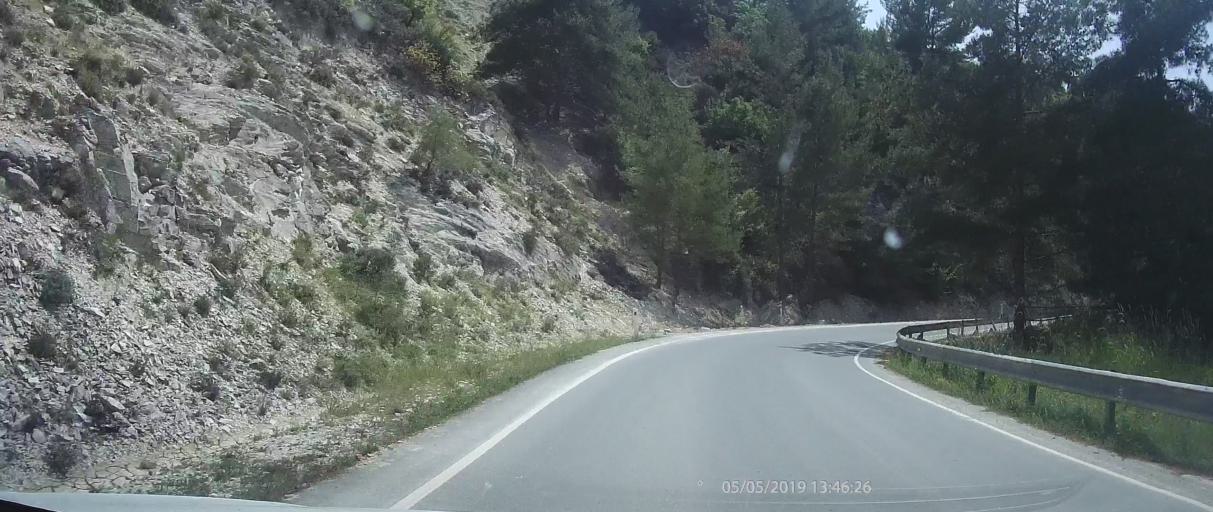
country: CY
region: Limassol
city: Pachna
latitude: 34.8709
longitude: 32.7721
